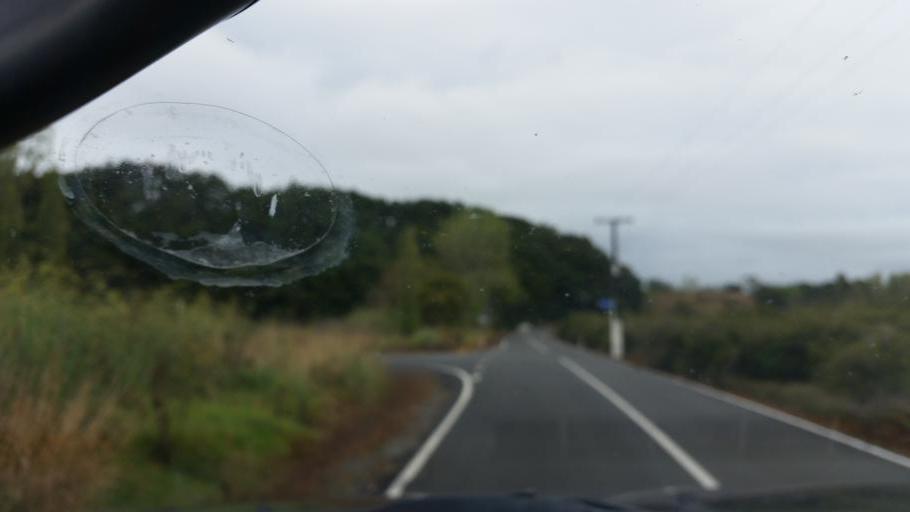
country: NZ
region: Auckland
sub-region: Auckland
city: Wellsford
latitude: -36.1223
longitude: 174.3617
